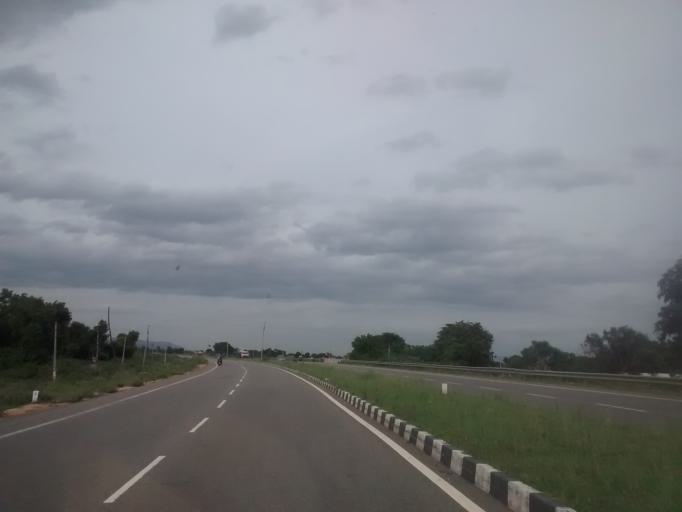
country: IN
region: Andhra Pradesh
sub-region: Chittoor
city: Narasingapuram
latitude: 13.5988
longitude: 79.3581
